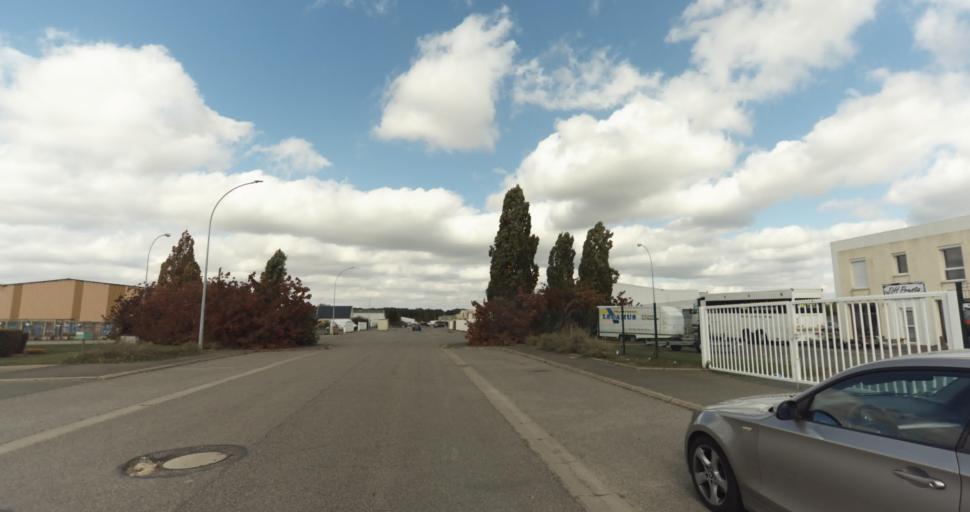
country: FR
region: Centre
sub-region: Departement d'Eure-et-Loir
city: Garnay
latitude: 48.7277
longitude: 1.3224
